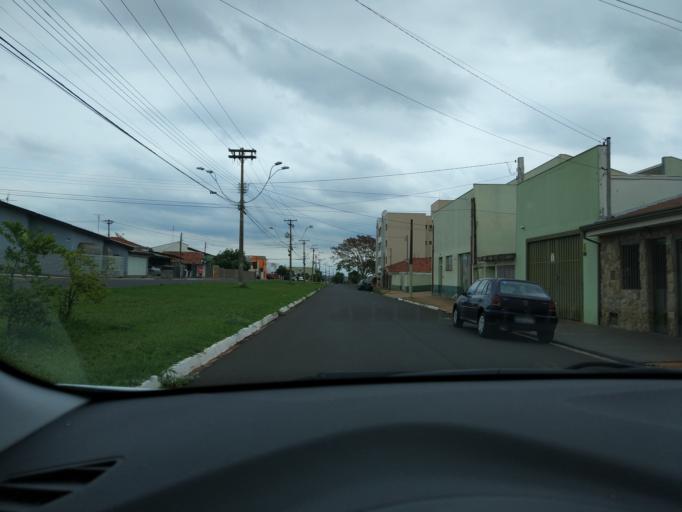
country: BR
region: Sao Paulo
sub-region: Jau
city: Jau
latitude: -22.2782
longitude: -48.5384
